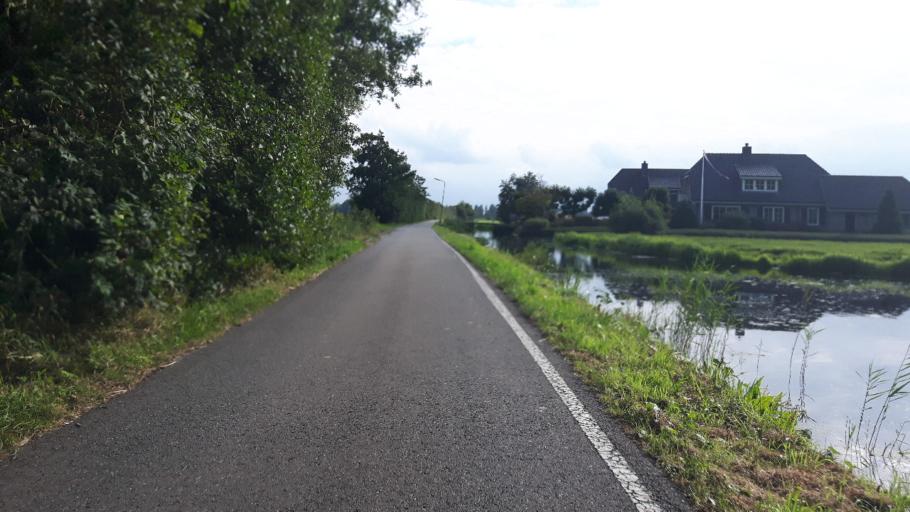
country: NL
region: Utrecht
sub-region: Gemeente De Ronde Venen
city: Mijdrecht
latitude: 52.1703
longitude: 4.9021
